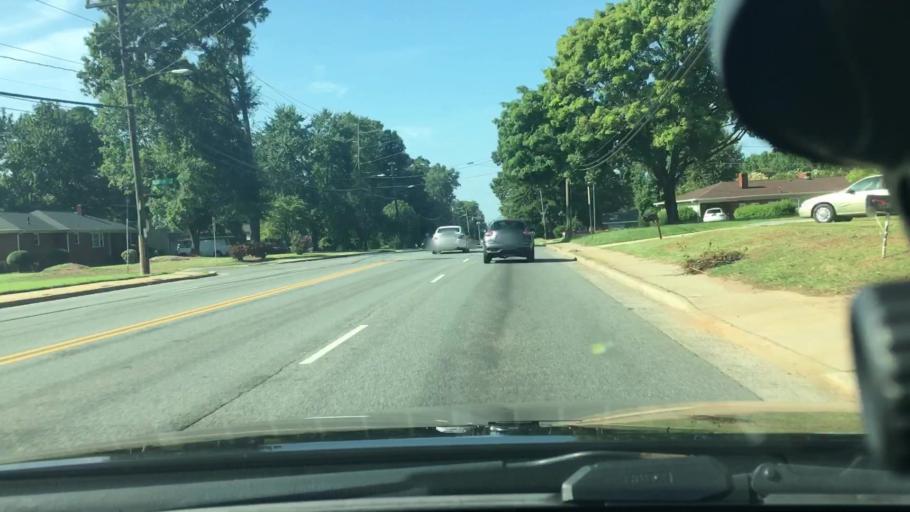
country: US
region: North Carolina
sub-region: Mecklenburg County
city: Matthews
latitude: 35.1926
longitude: -80.7264
